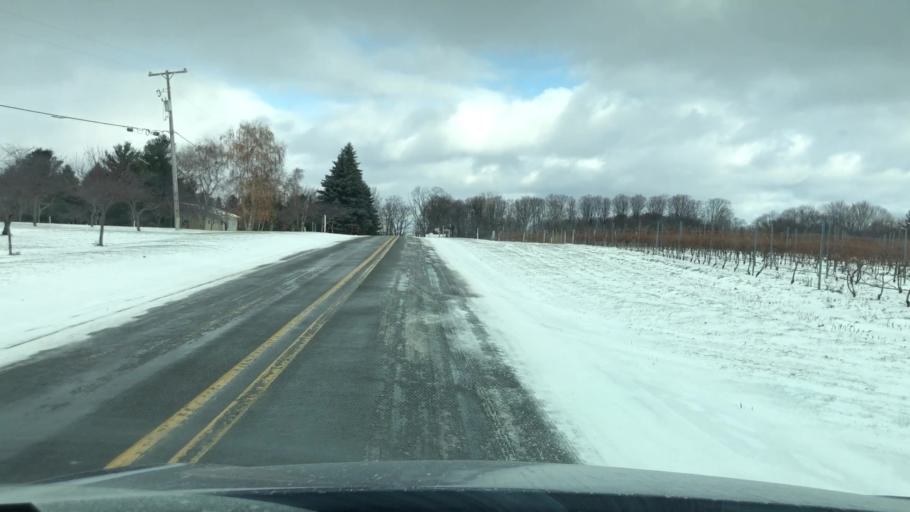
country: US
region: Michigan
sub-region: Antrim County
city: Elk Rapids
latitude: 44.9216
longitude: -85.4984
